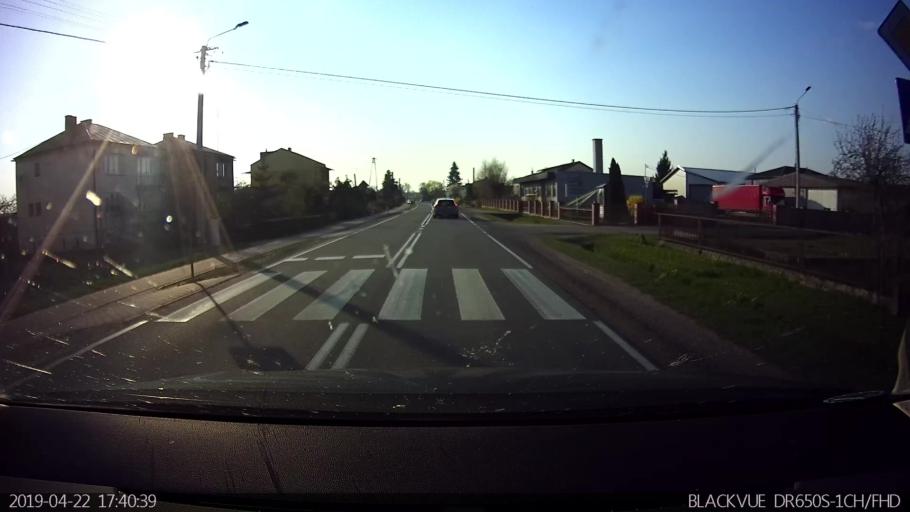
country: PL
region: Masovian Voivodeship
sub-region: Powiat wegrowski
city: Miedzna
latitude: 52.3994
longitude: 22.1222
